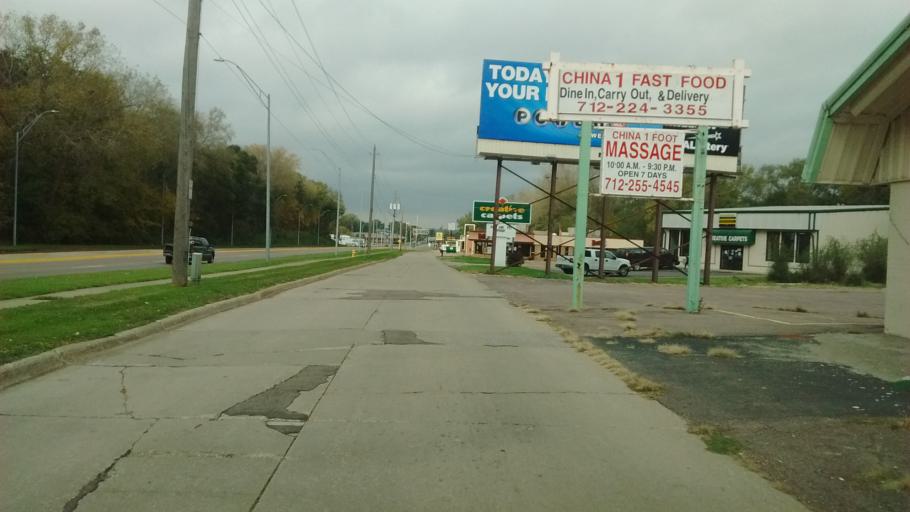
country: US
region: Iowa
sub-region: Woodbury County
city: Sioux City
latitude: 42.4846
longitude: -96.3565
